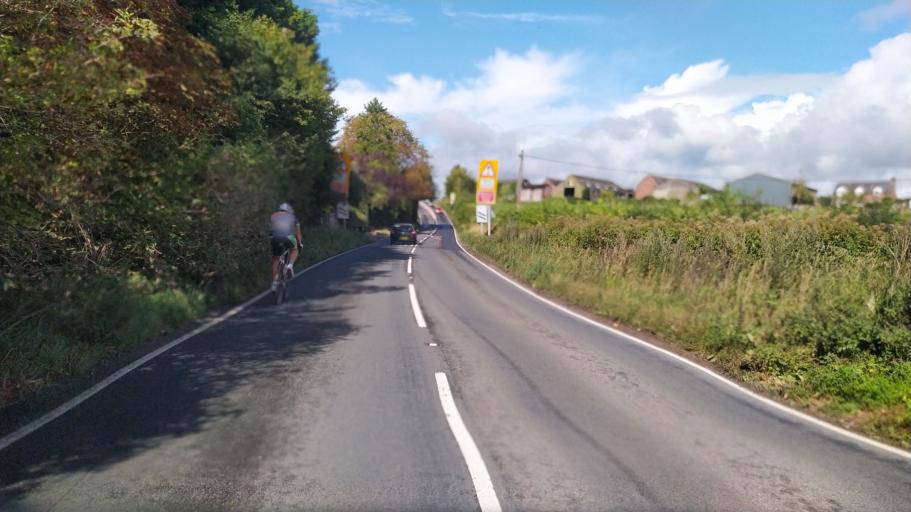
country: GB
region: England
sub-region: Dorset
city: Blandford Forum
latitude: 50.8885
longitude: -2.2226
